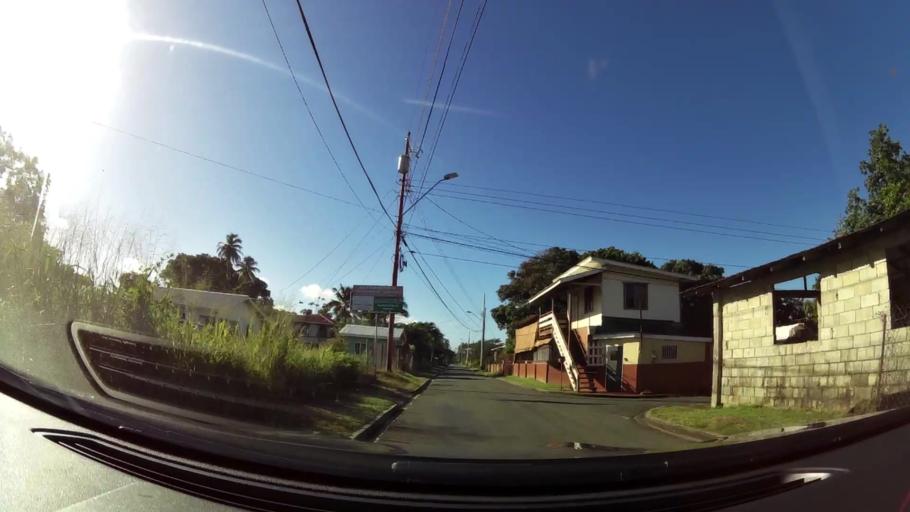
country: TT
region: Tobago
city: Scarborough
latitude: 11.1564
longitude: -60.8205
